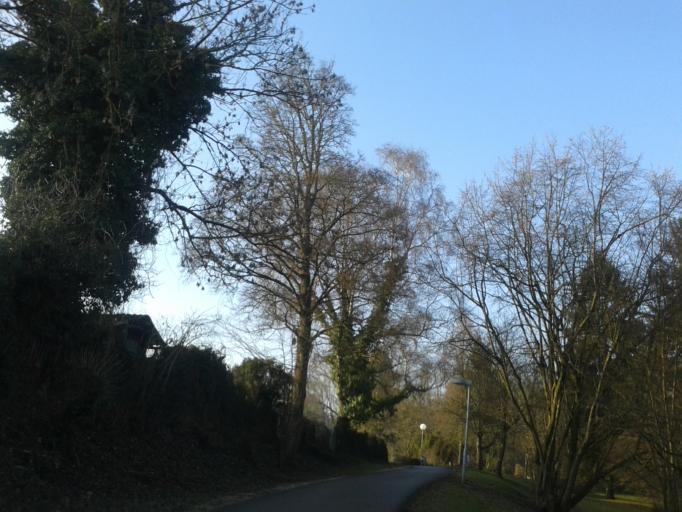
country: DE
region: Baden-Wuerttemberg
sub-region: Tuebingen Region
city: Ulm
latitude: 48.3939
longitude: 9.9878
